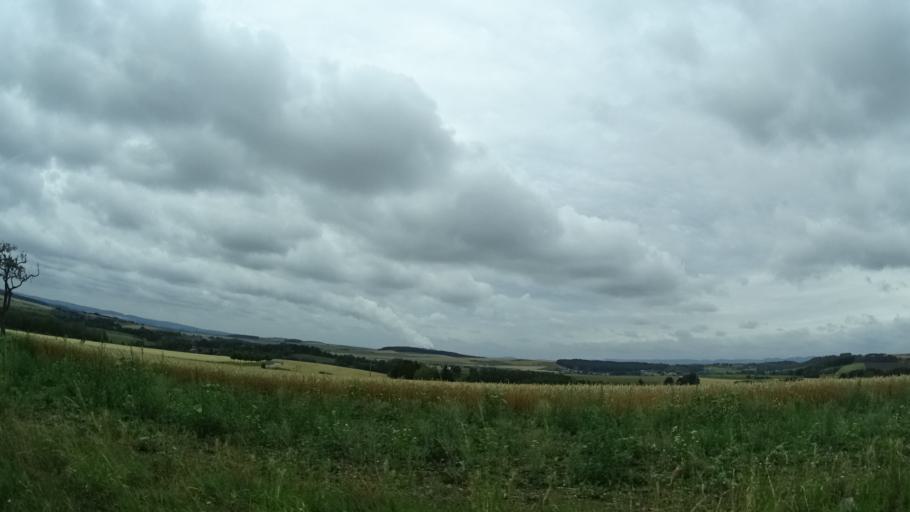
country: LU
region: Grevenmacher
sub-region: Canton de Remich
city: Mondorf-les-Bains
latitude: 49.4956
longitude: 6.2929
